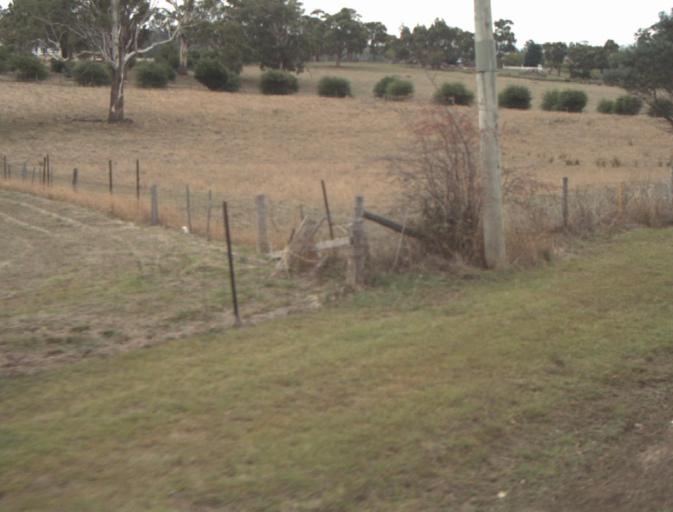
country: AU
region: Tasmania
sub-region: Launceston
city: Summerhill
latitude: -41.4999
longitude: 147.1896
